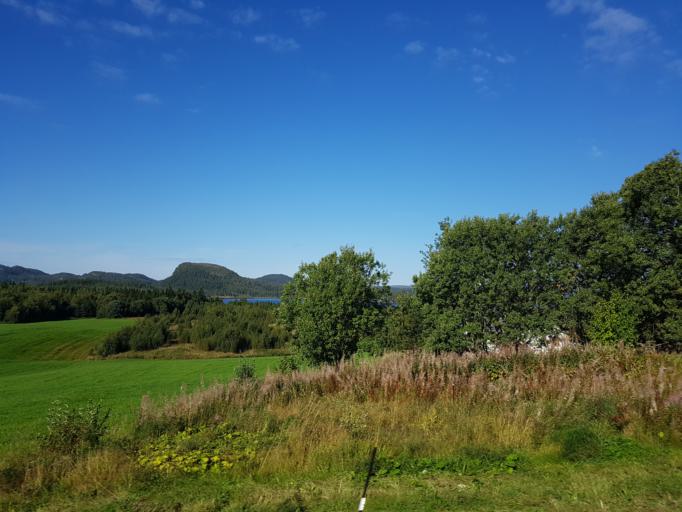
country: NO
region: Sor-Trondelag
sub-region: Trondheim
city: Trondheim
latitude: 63.6024
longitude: 10.2255
